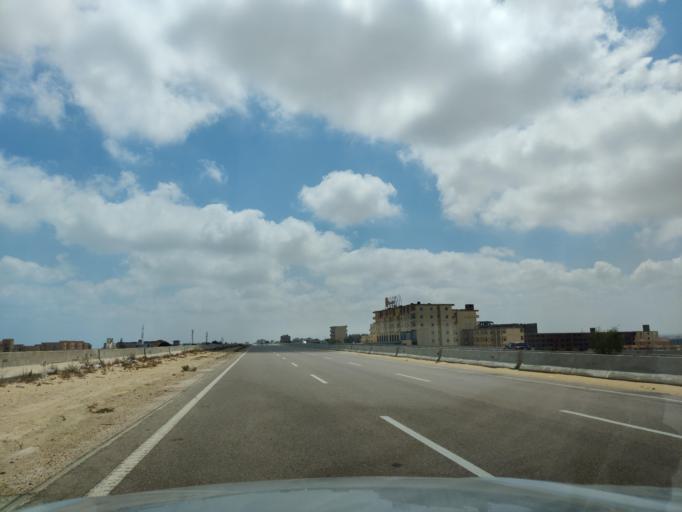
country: EG
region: Muhafazat Matruh
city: Al `Alamayn
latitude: 30.8191
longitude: 29.1585
